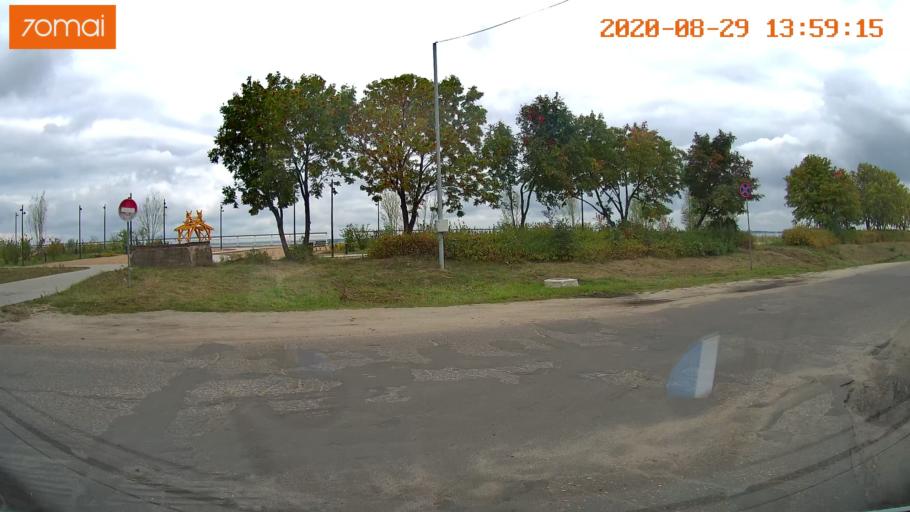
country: RU
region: Ivanovo
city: Yur'yevets
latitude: 57.3162
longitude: 43.1133
